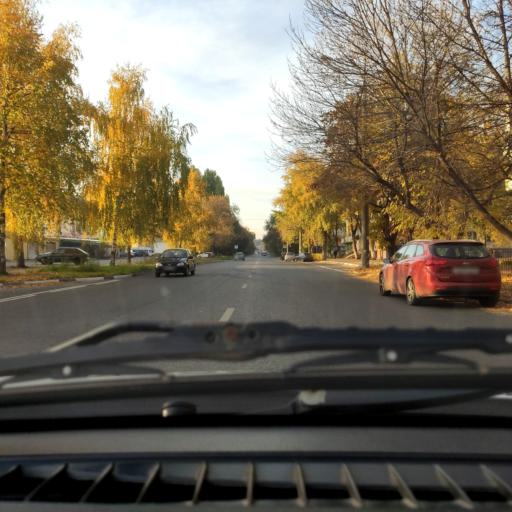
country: RU
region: Samara
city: Tol'yatti
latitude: 53.5266
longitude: 49.4295
